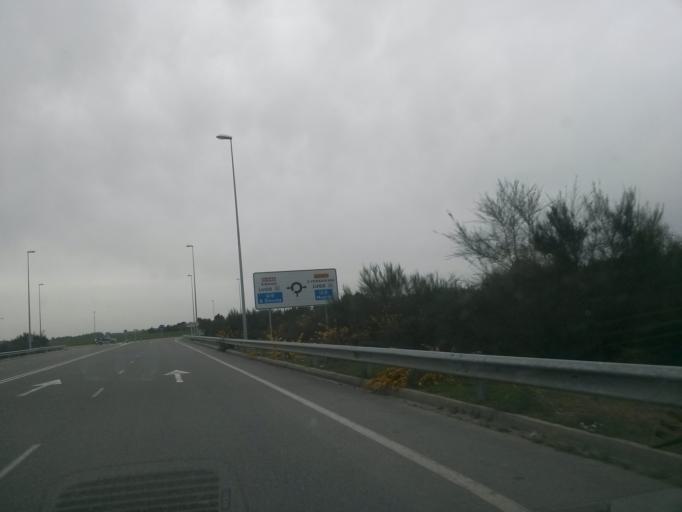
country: ES
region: Galicia
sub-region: Provincia de Lugo
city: Lugo
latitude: 43.0246
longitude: -7.5331
